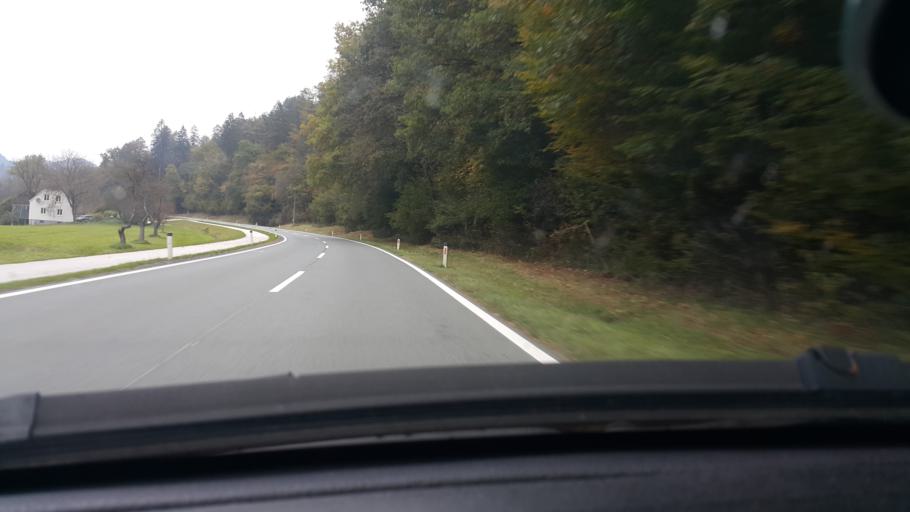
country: AT
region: Carinthia
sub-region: Politischer Bezirk Wolfsberg
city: Lavamund
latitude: 46.6183
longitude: 14.9753
